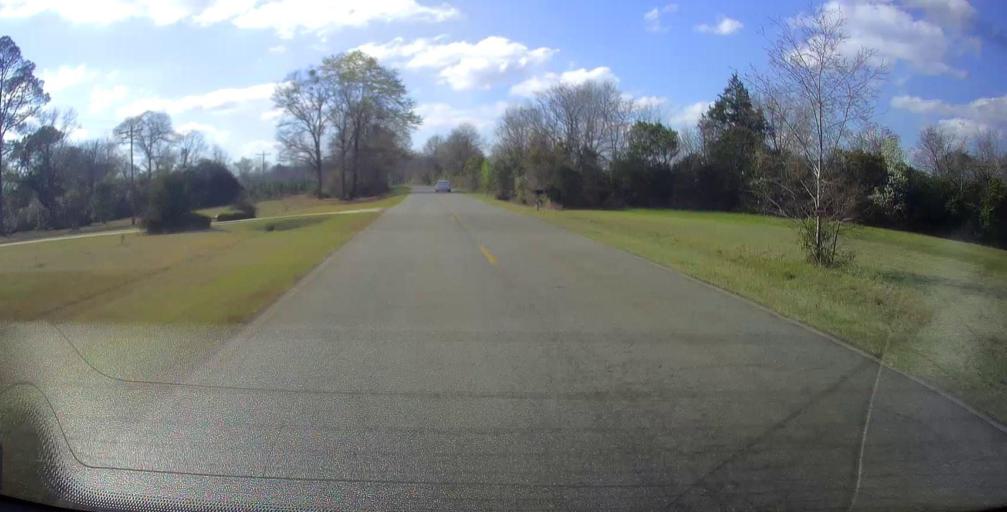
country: US
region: Georgia
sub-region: Wilkinson County
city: Irwinton
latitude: 32.6353
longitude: -83.1244
